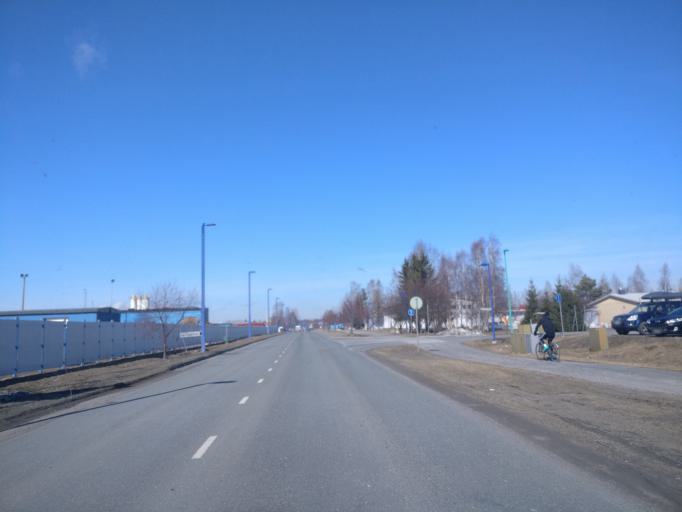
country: FI
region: Lapland
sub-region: Kemi-Tornio
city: Kemi
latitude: 65.7341
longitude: 24.5844
